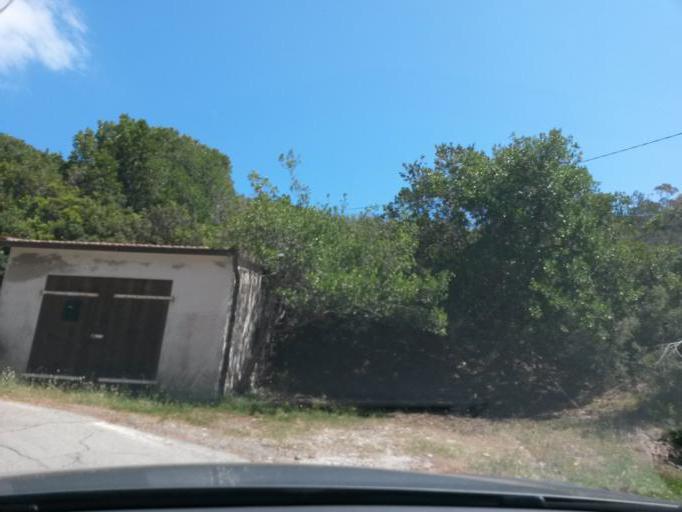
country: IT
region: Tuscany
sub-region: Provincia di Livorno
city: Marciana
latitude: 42.7932
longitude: 10.1128
